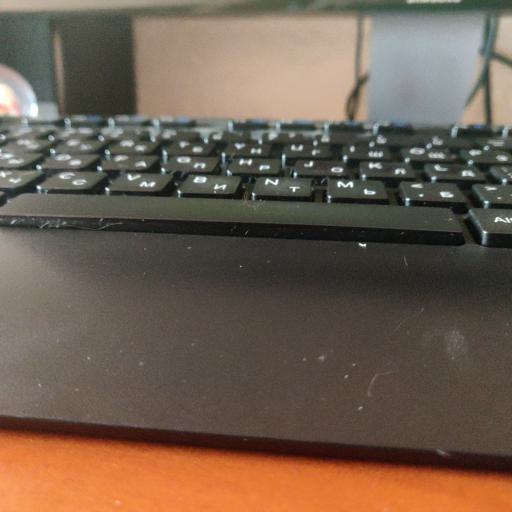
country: FI
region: Haeme
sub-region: Forssa
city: Ypaejae
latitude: 60.7958
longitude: 23.2499
